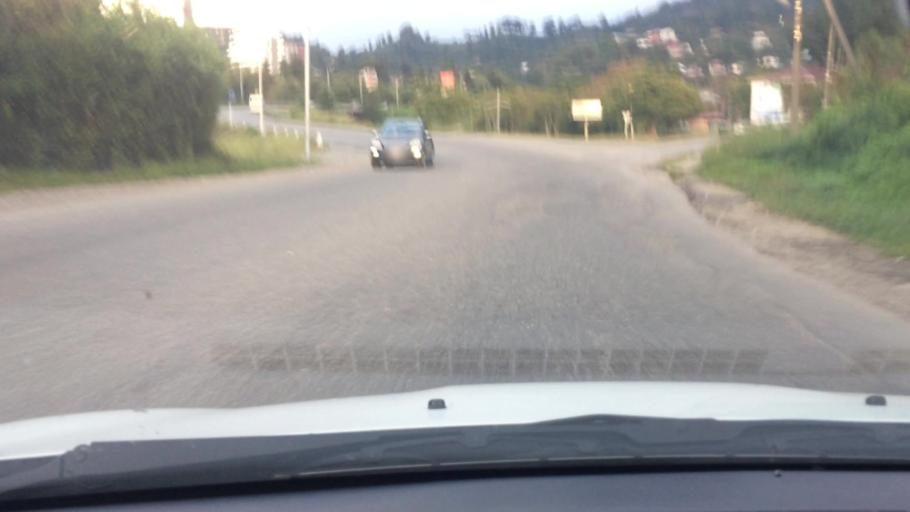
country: GE
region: Ajaria
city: Makhinjauri
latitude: 41.6860
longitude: 41.7025
